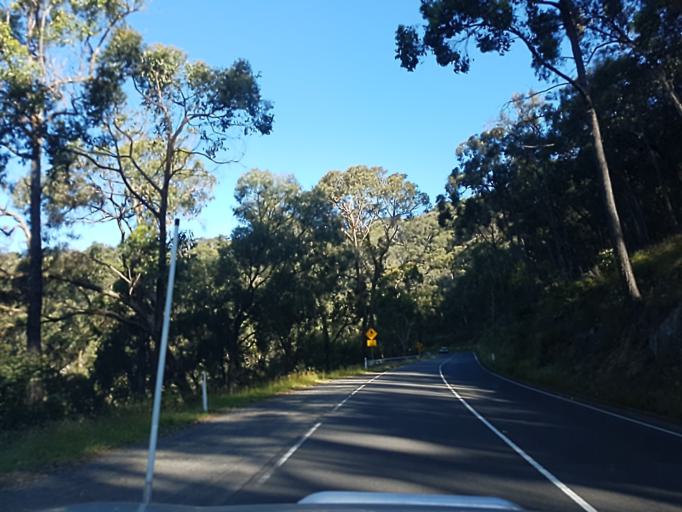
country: AU
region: Victoria
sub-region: Yarra Ranges
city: Kalorama
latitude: -37.8101
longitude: 145.3730
